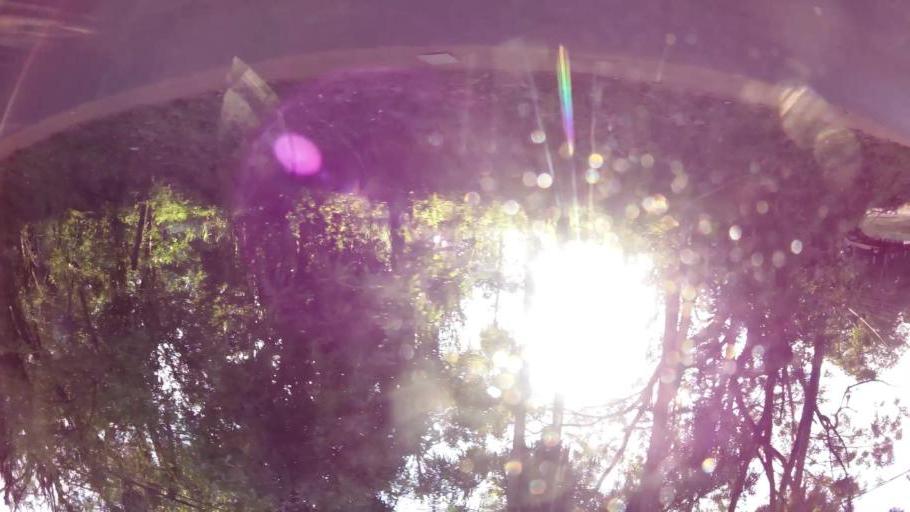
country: PY
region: Central
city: Fernando de la Mora
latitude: -25.3547
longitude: -57.5282
